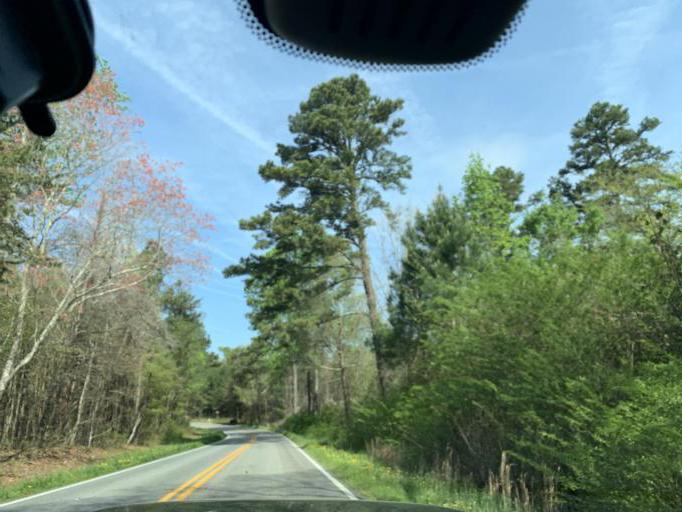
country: US
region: Georgia
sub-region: Forsyth County
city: Cumming
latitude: 34.2071
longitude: -84.0699
